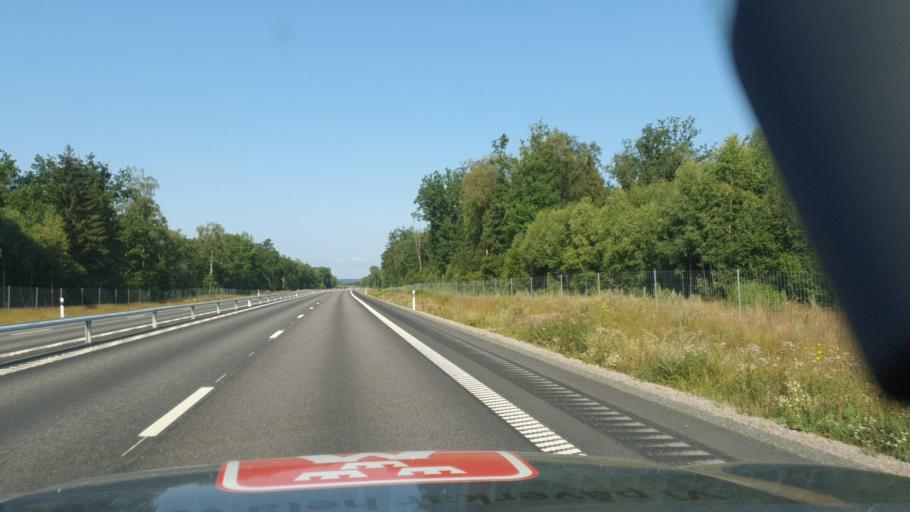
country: SE
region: Skane
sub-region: Kristianstads Kommun
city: Onnestad
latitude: 55.9610
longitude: 13.9784
